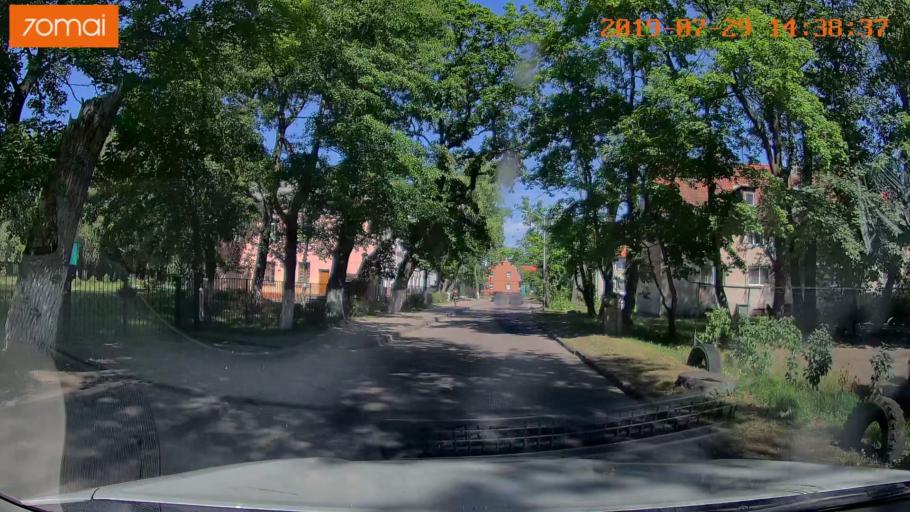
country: RU
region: Kaliningrad
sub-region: Gorod Kaliningrad
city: Baltiysk
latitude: 54.6500
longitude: 19.9021
